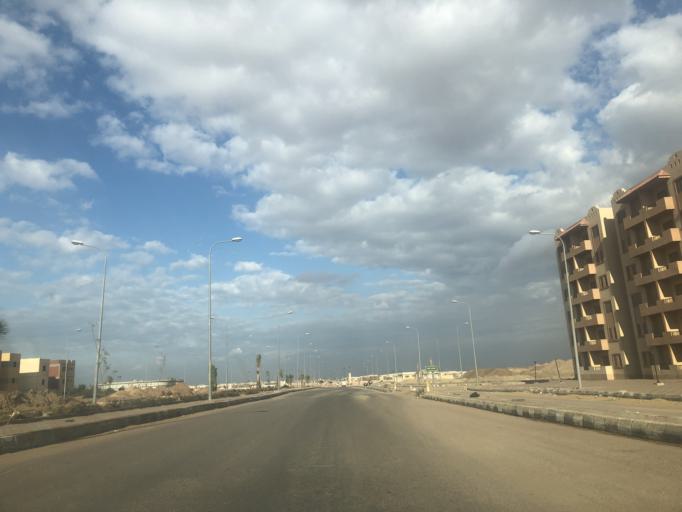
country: EG
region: Al Jizah
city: Madinat Sittah Uktubar
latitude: 29.9274
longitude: 31.0353
